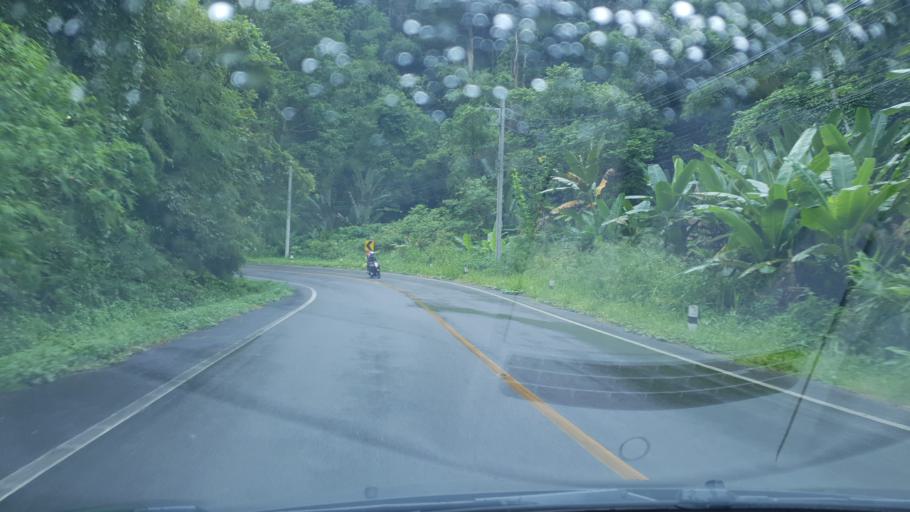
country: TH
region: Mae Hong Son
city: Mae La Noi
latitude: 18.6077
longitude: 97.9403
